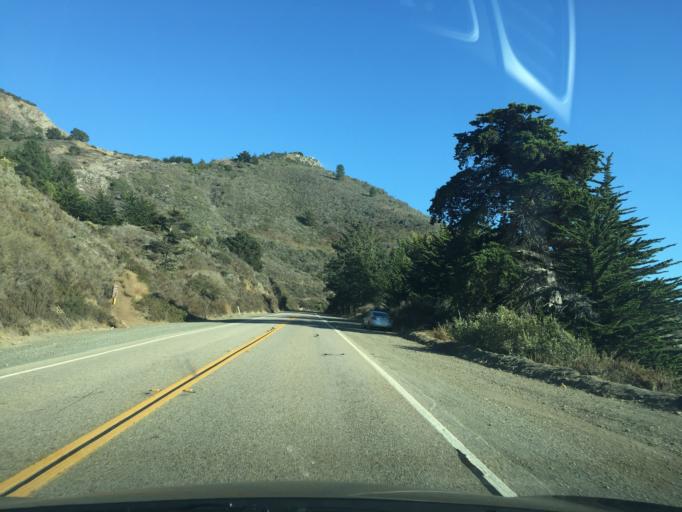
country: US
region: California
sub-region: San Luis Obispo County
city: Cambria
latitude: 35.8432
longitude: -121.4032
